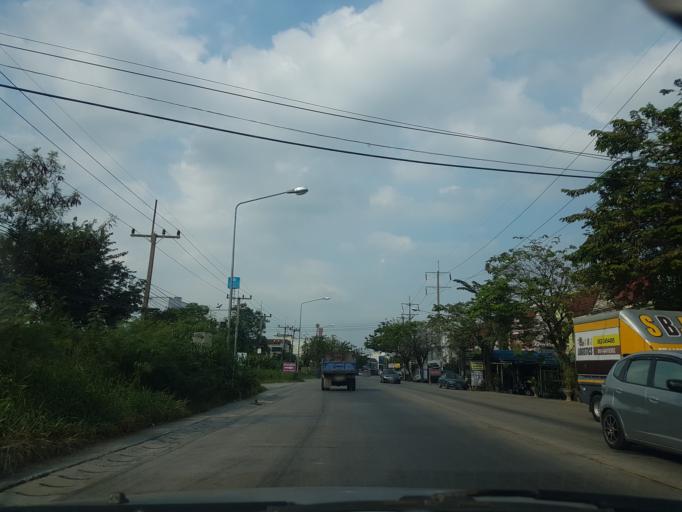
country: TH
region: Phra Nakhon Si Ayutthaya
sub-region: Amphoe Tha Ruea
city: Tha Ruea
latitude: 14.5673
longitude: 100.7257
